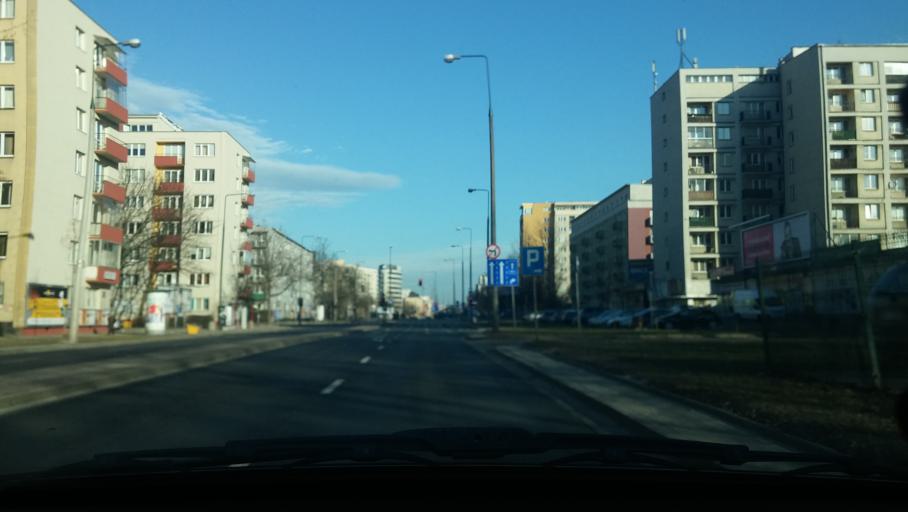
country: PL
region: Masovian Voivodeship
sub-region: Warszawa
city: Mokotow
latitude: 52.1858
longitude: 21.0191
